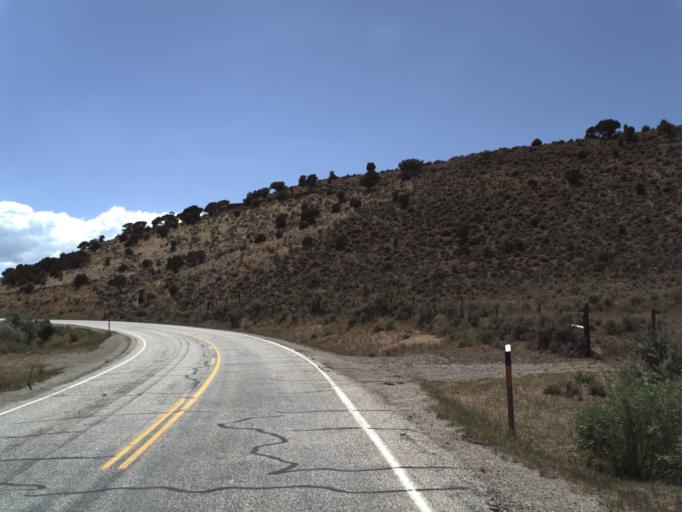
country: US
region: Utah
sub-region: Rich County
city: Randolph
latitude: 41.5032
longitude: -111.2446
